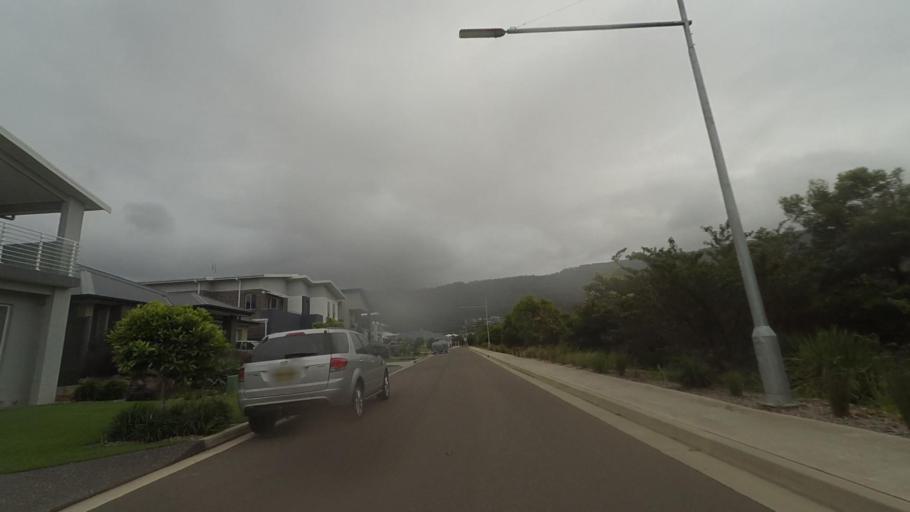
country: AU
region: New South Wales
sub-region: Wollongong
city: Bulli
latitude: -34.3223
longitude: 150.9199
